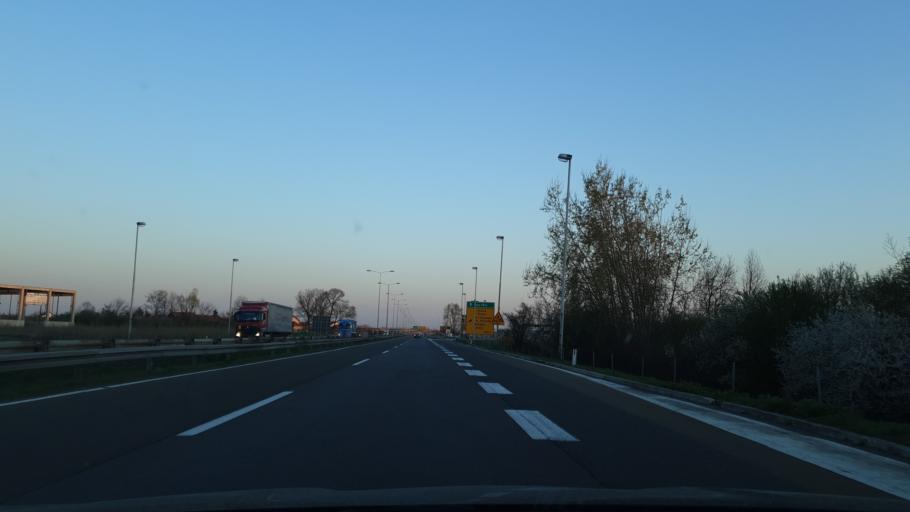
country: RS
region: Central Serbia
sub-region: Podunavski Okrug
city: Velika Plana
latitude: 44.3475
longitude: 21.0770
